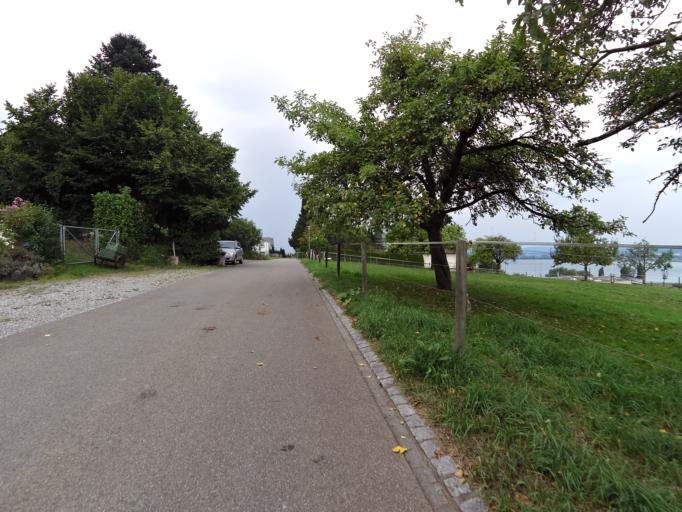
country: CH
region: Thurgau
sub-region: Kreuzlingen District
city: Tagerwilen
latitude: 47.6592
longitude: 9.1094
